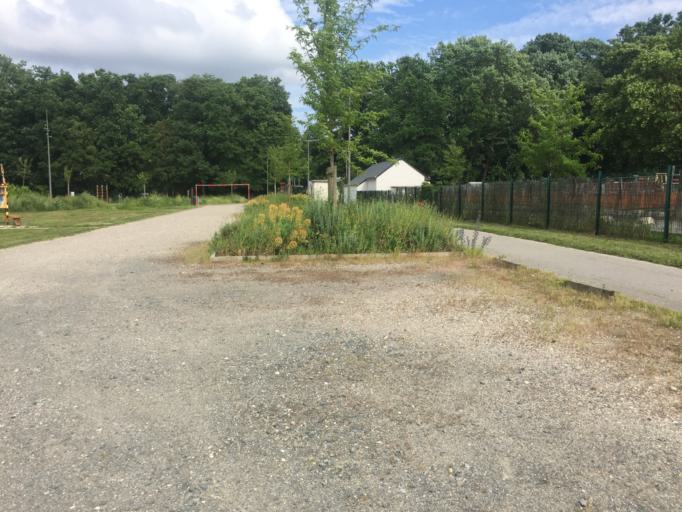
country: FR
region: Centre
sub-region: Departement d'Indre-et-Loire
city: Chambray-les-Tours
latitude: 47.3394
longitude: 0.7161
